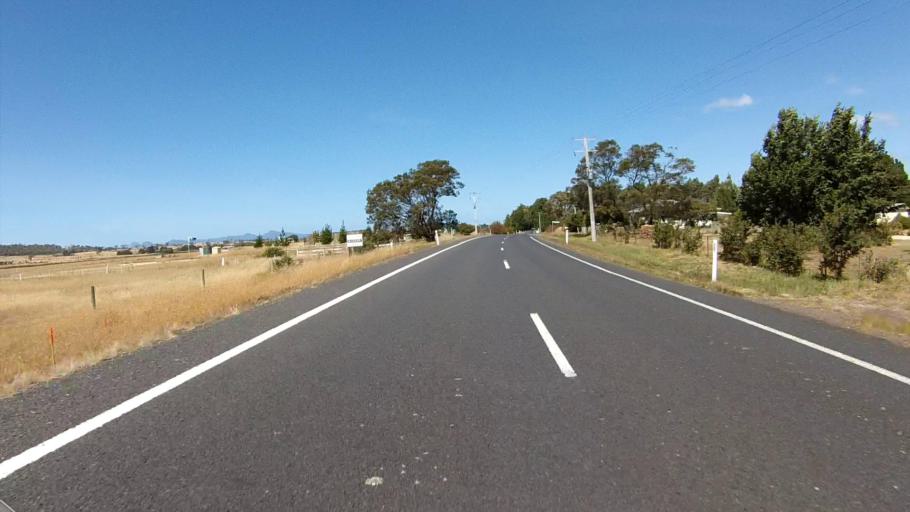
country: AU
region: Tasmania
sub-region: Break O'Day
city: St Helens
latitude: -42.0585
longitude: 148.0604
